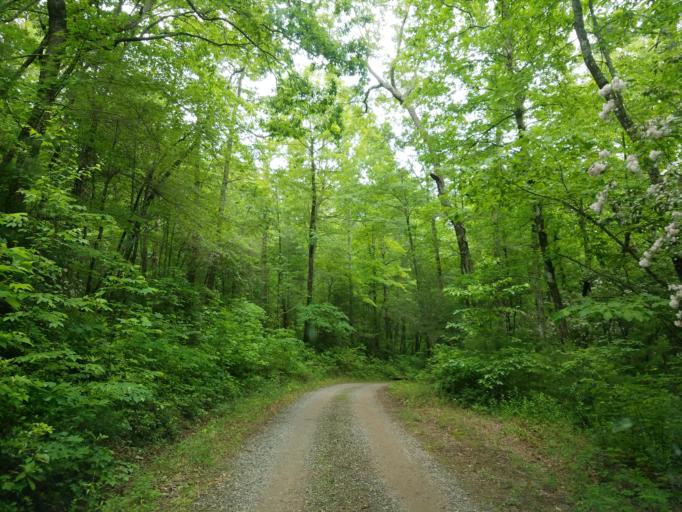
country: US
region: Georgia
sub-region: Lumpkin County
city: Dahlonega
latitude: 34.6737
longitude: -83.9753
